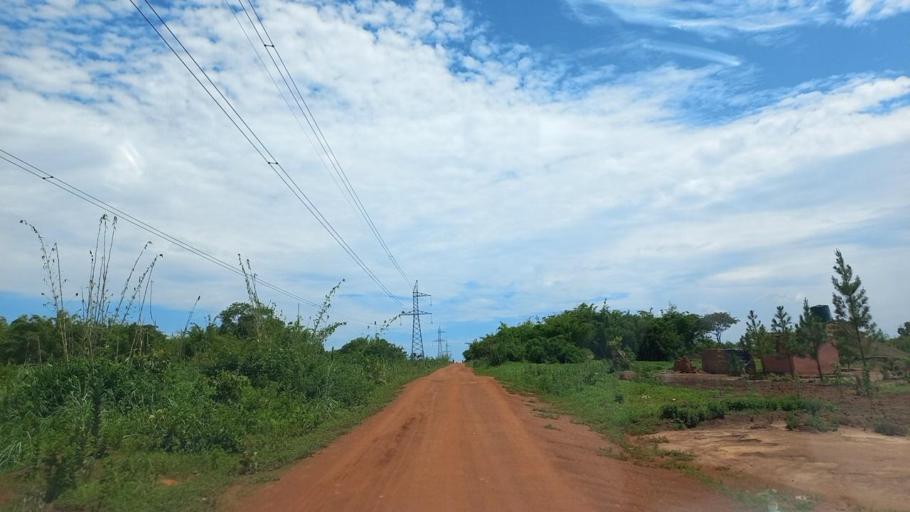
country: ZM
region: Copperbelt
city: Kitwe
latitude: -12.8064
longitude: 28.3623
